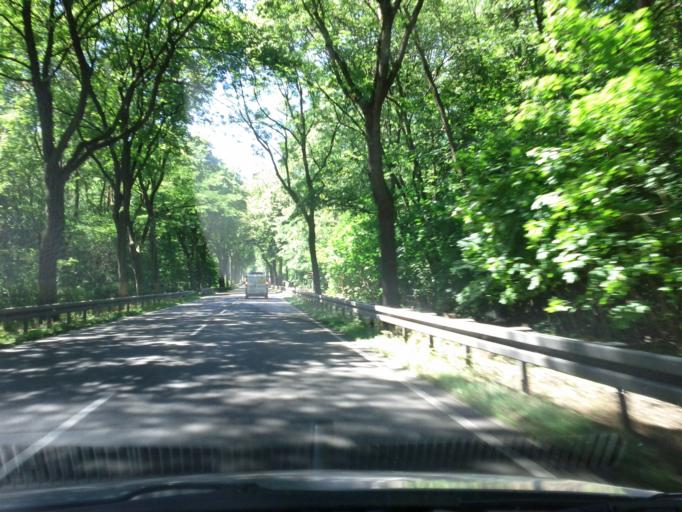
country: DE
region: Brandenburg
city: Rehfelde
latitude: 52.4805
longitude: 13.9200
